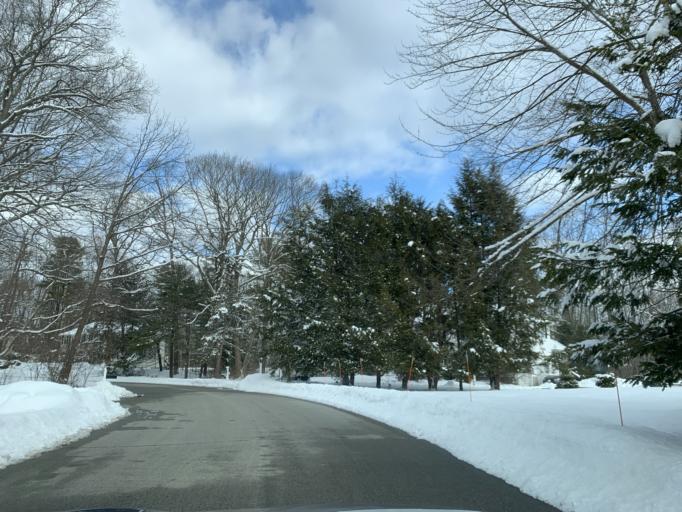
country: US
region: Massachusetts
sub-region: Norfolk County
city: Dover
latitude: 42.2568
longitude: -71.2910
